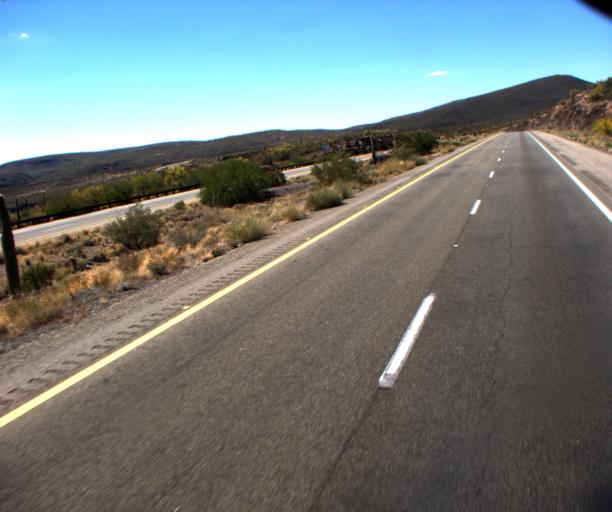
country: US
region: Arizona
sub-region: Yavapai County
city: Bagdad
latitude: 34.5394
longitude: -113.4353
